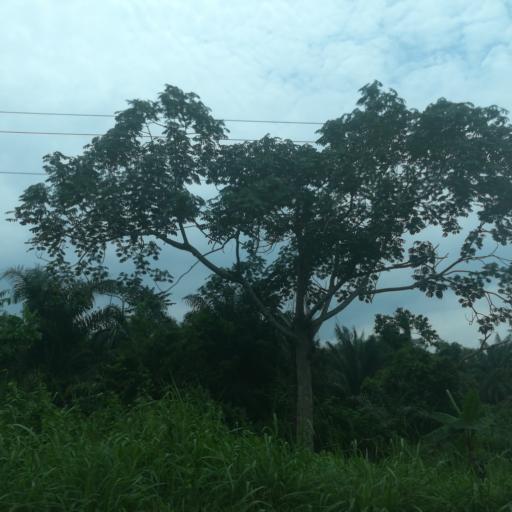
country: NG
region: Lagos
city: Ejirin
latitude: 6.6494
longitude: 3.7847
